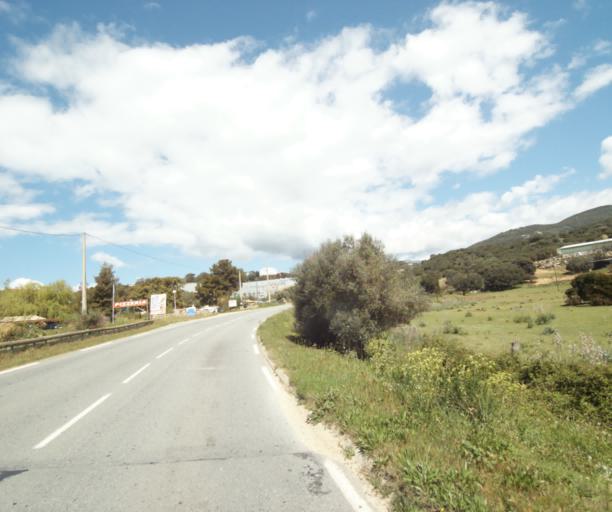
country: FR
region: Corsica
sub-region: Departement de la Corse-du-Sud
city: Propriano
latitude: 41.6602
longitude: 8.9170
